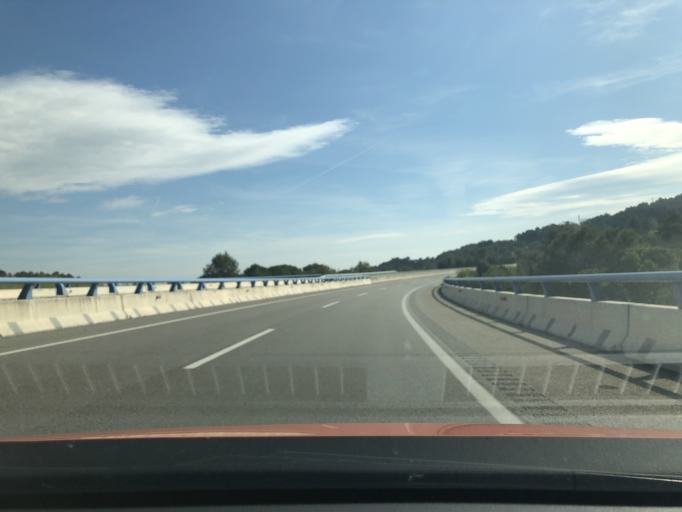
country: ES
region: Catalonia
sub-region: Provincia de Barcelona
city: Navas
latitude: 41.9184
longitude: 1.8848
